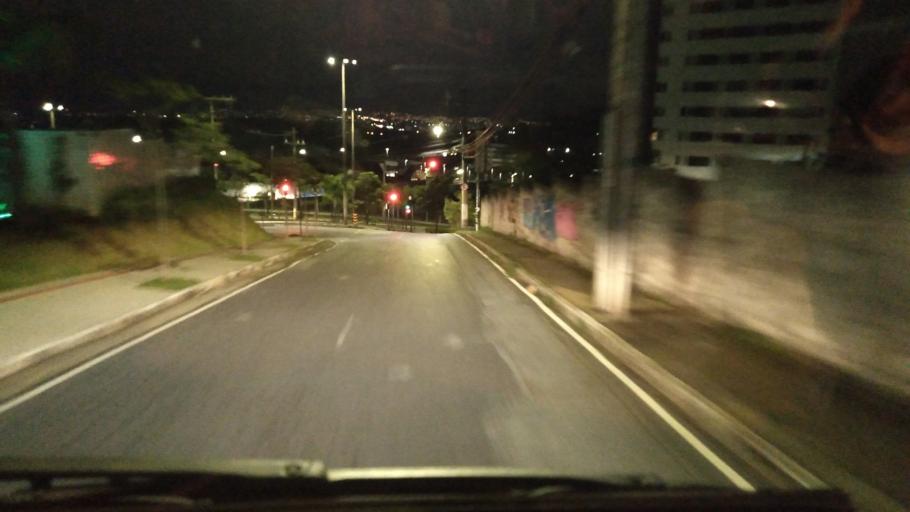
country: BR
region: Minas Gerais
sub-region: Belo Horizonte
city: Belo Horizonte
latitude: -19.8930
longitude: -43.9683
